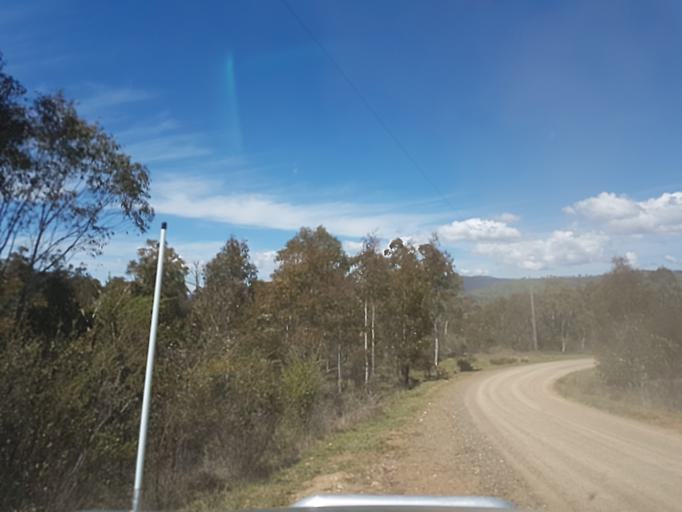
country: AU
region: Victoria
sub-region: Alpine
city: Mount Beauty
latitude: -37.0854
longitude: 147.4070
